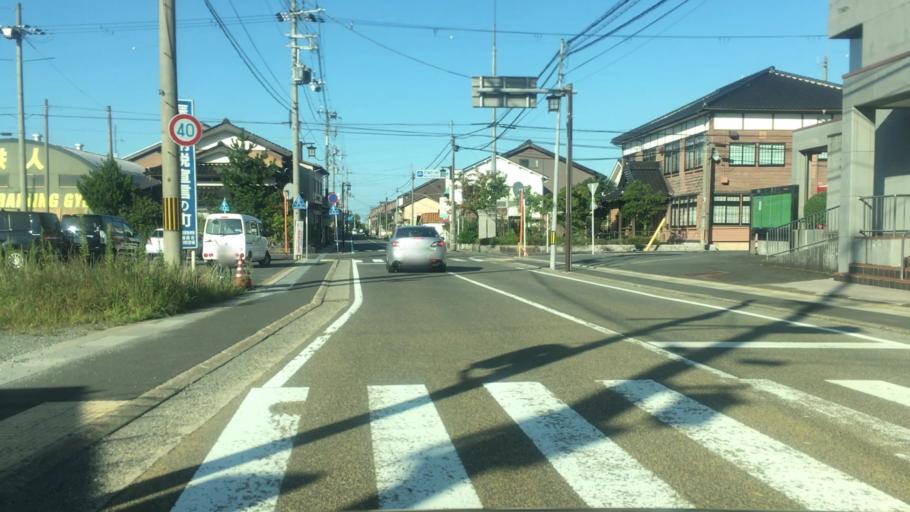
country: JP
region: Hyogo
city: Toyooka
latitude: 35.6035
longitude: 134.8947
